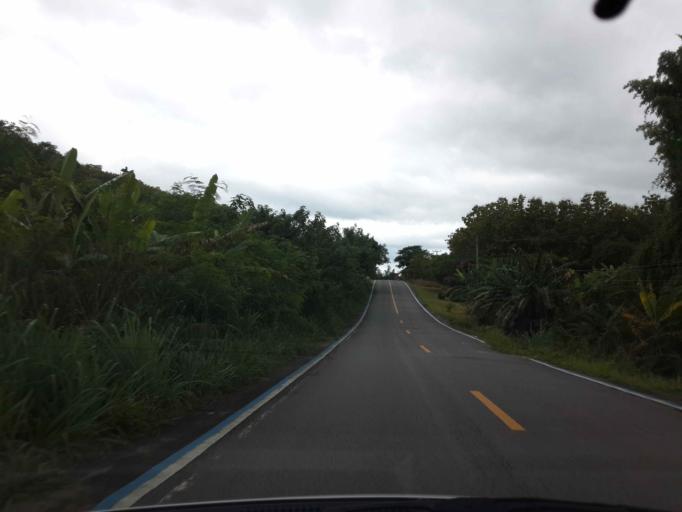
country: TH
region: Ratchaburi
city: Suan Phueng
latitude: 13.6183
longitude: 99.2254
